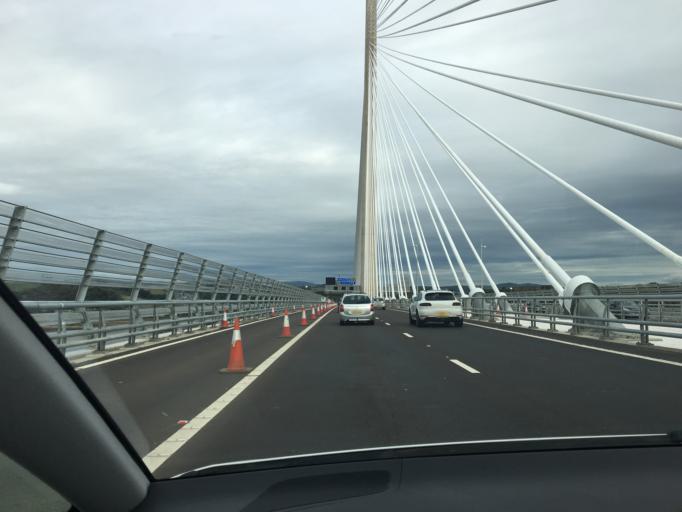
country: GB
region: Scotland
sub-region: Fife
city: North Queensferry
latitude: 56.0081
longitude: -3.4108
